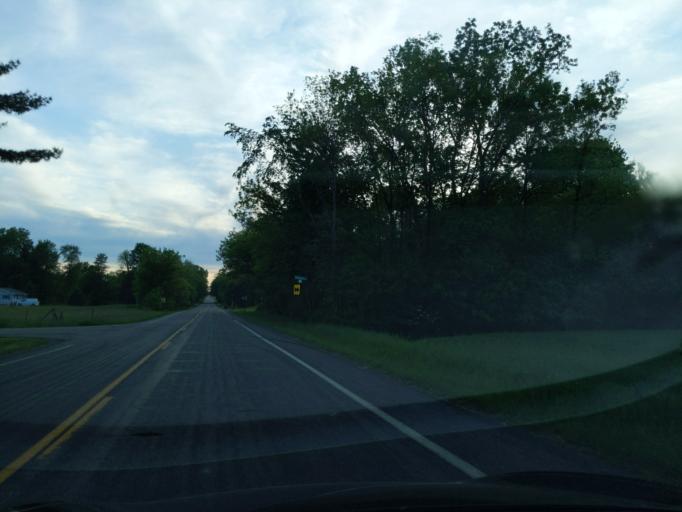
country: US
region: Michigan
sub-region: Ingham County
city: Williamston
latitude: 42.6009
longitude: -84.3279
